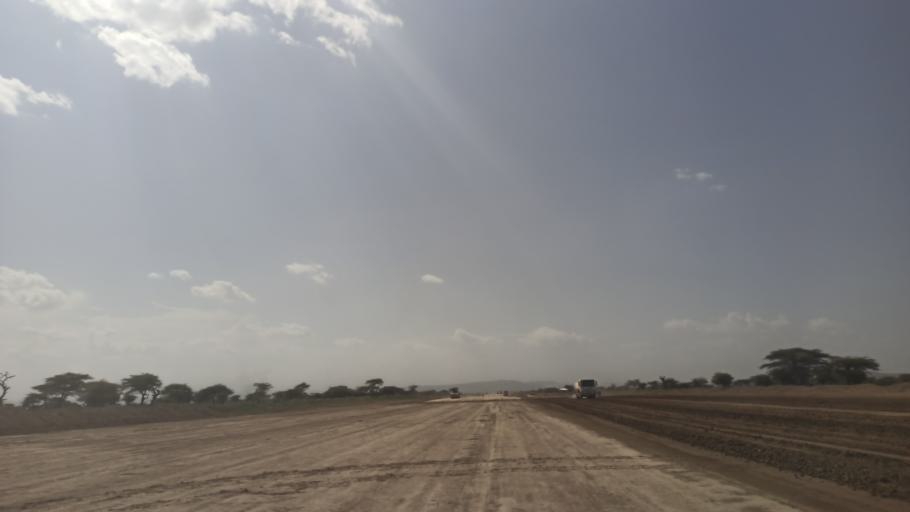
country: ET
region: Oromiya
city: Ziway
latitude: 7.7142
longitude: 38.6342
